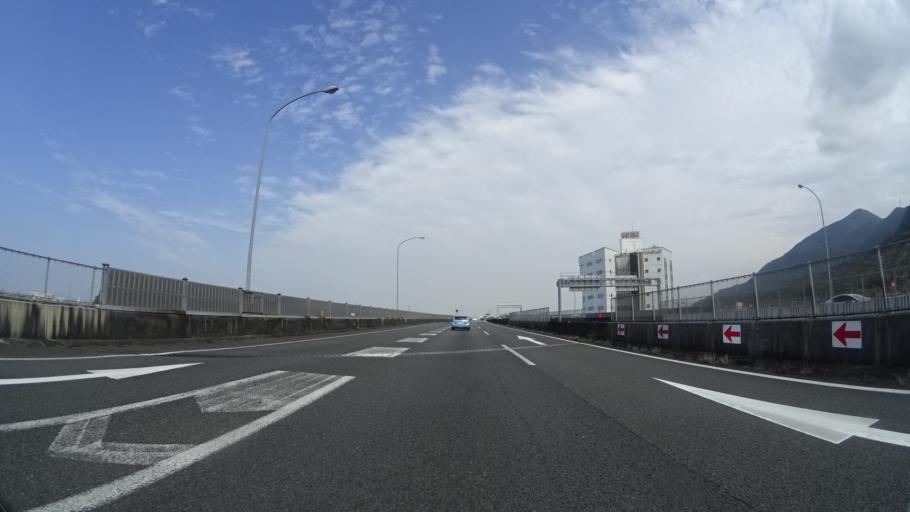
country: JP
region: Kumamoto
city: Yatsushiro
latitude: 32.5051
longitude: 130.6461
